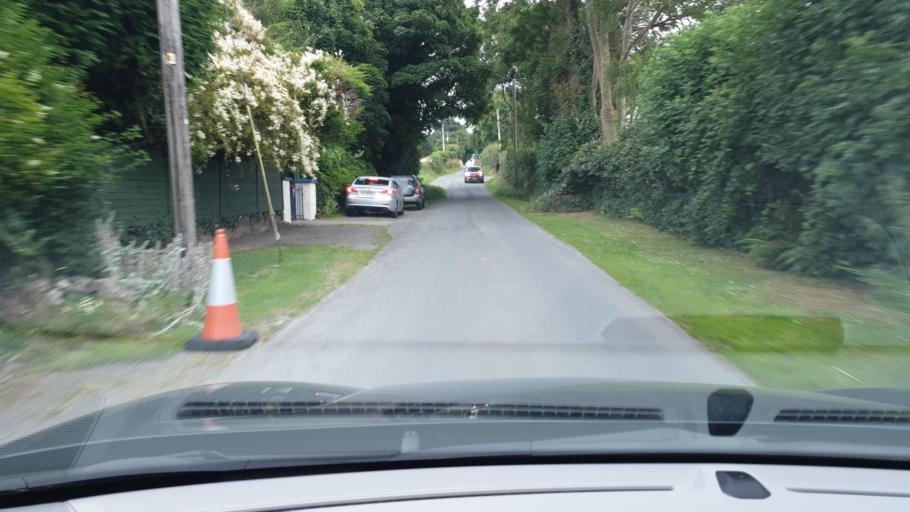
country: IE
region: Leinster
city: Balrothery
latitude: 53.5764
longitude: -6.1743
